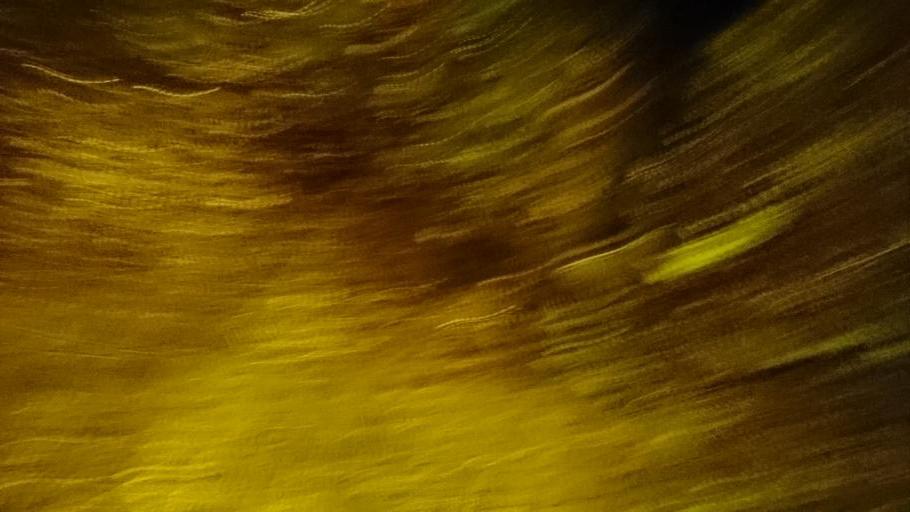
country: NO
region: Telemark
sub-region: Kragero
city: Kragero
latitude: 58.8664
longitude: 9.4007
